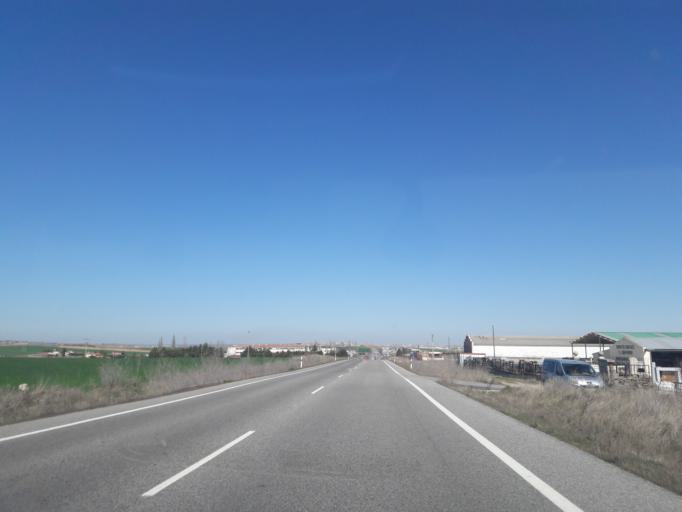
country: ES
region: Castille and Leon
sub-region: Provincia de Salamanca
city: Miranda de Azan
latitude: 40.8895
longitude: -5.6642
